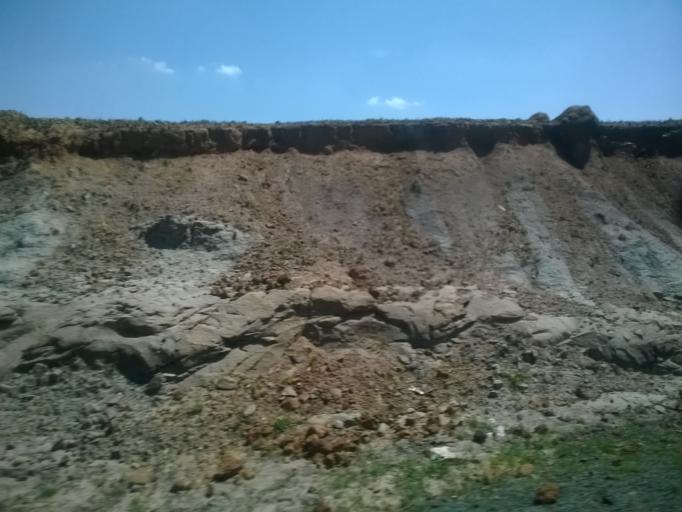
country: LS
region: Berea
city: Teyateyaneng
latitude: -29.1028
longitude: 27.8479
